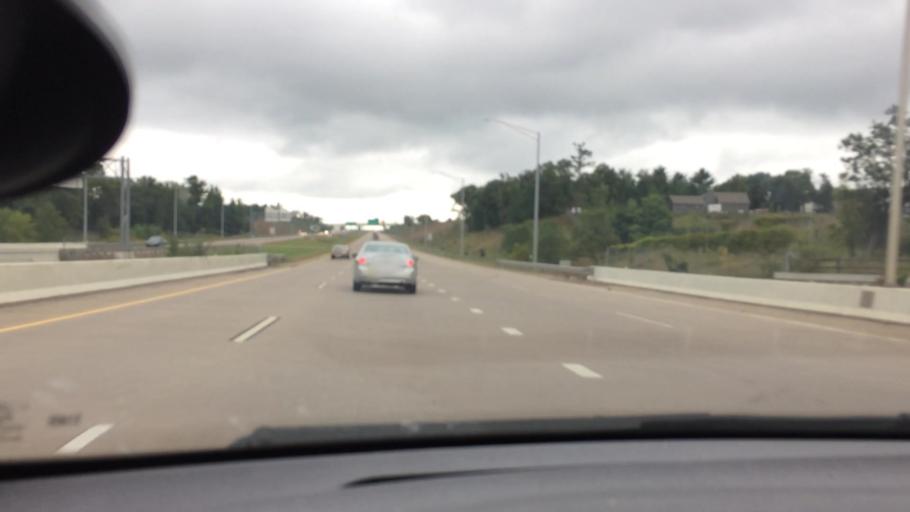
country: US
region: Wisconsin
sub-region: Eau Claire County
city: Altoona
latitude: 44.7994
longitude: -91.4557
